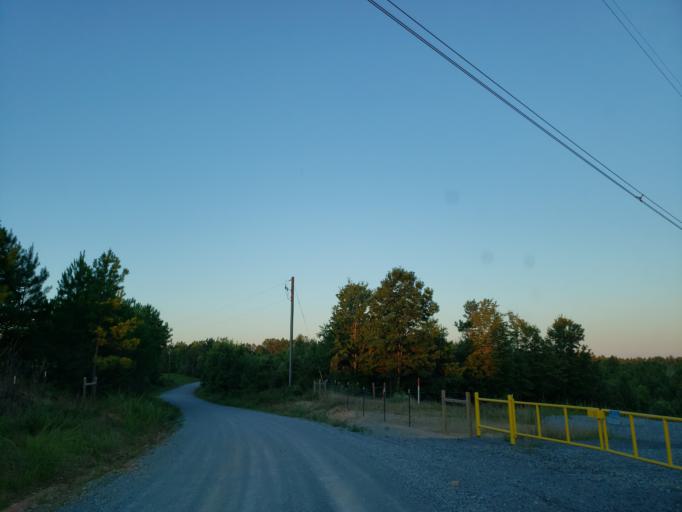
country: US
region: Georgia
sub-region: Bartow County
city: Cartersville
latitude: 34.0595
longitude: -84.8521
